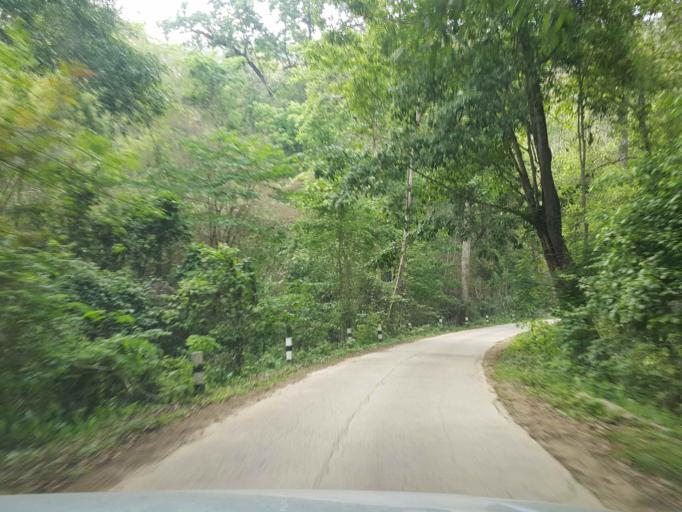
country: TH
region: Chiang Mai
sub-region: Amphoe Chiang Dao
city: Chiang Dao
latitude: 19.4099
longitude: 98.7901
